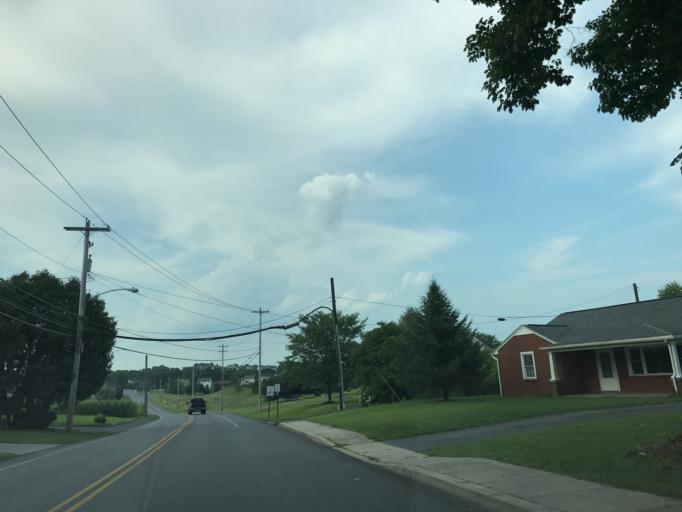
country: US
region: Pennsylvania
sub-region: Lancaster County
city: Mount Joy
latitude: 40.1075
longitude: -76.5325
